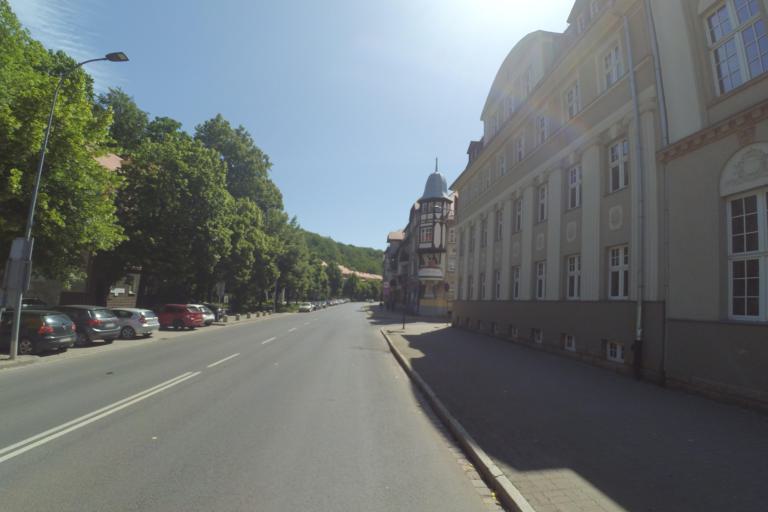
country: PL
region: Lower Silesian Voivodeship
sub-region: Powiat walbrzyski
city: Walbrzych
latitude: 50.7707
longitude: 16.2787
